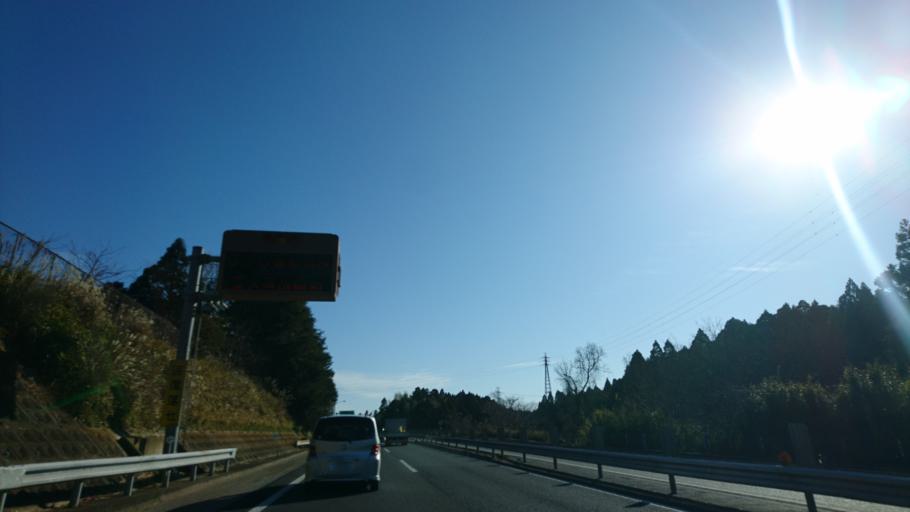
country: JP
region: Chiba
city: Oami
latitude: 35.5715
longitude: 140.2856
